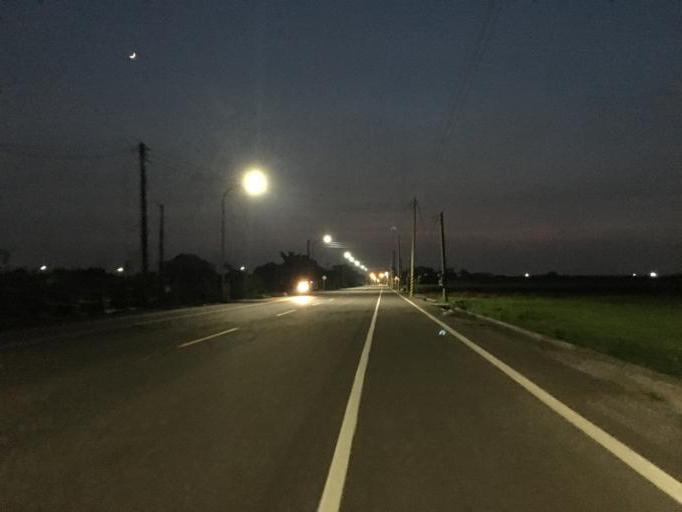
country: TW
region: Taiwan
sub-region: Chiayi
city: Taibao
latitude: 23.5178
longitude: 120.3116
